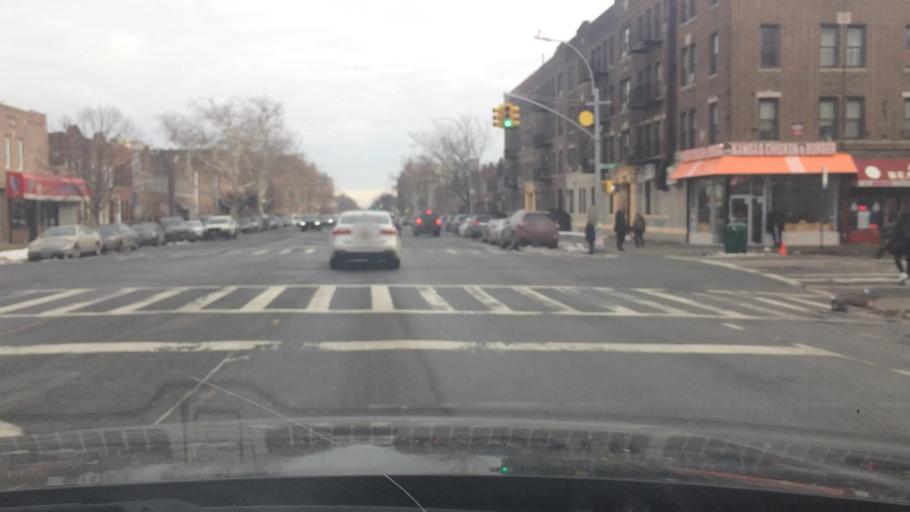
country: US
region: New York
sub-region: Kings County
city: Brooklyn
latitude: 40.6646
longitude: -73.9240
